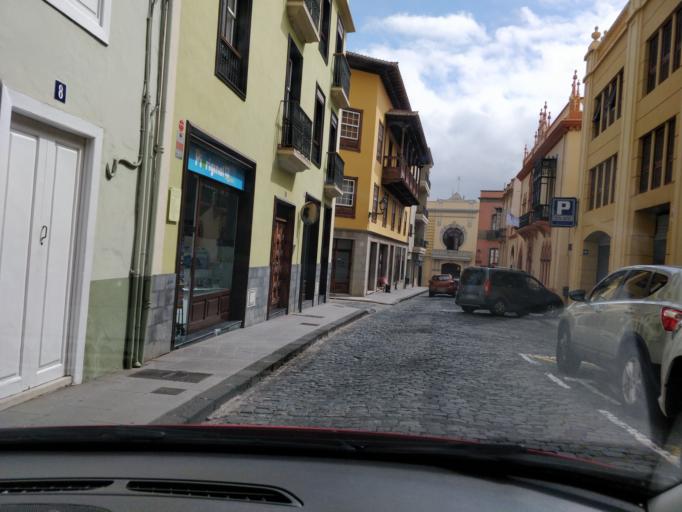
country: ES
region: Canary Islands
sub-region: Provincia de Santa Cruz de Tenerife
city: La Orotava
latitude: 28.3903
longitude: -16.5249
